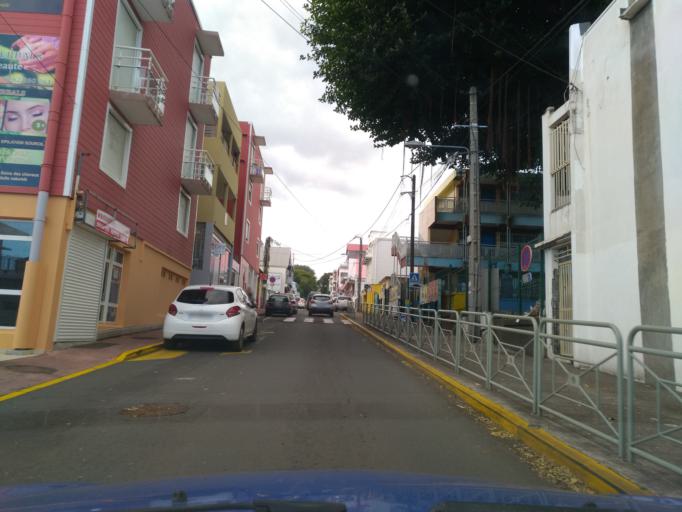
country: RE
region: Reunion
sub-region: Reunion
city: Saint-Pierre
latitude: -21.3370
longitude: 55.4765
